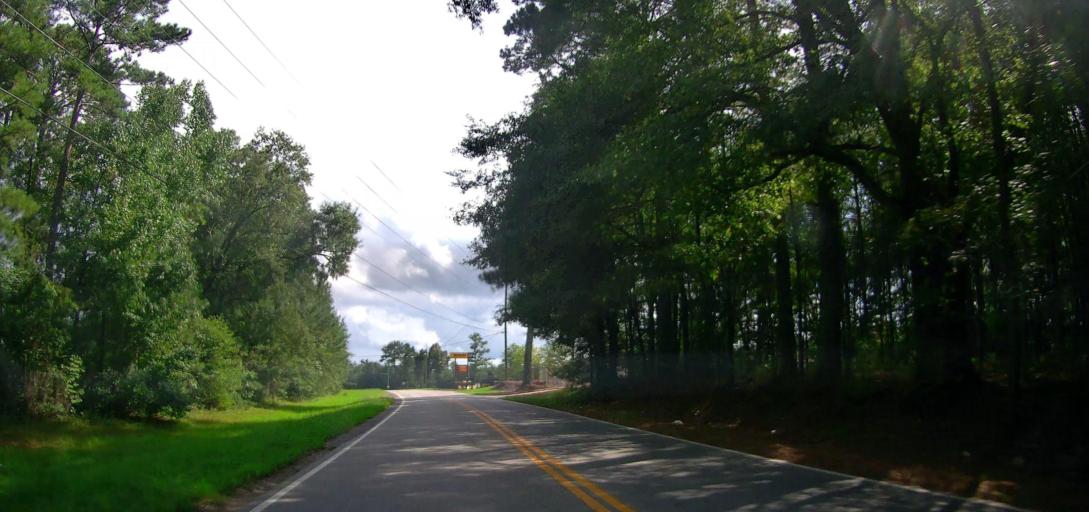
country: US
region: Alabama
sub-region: Russell County
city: Phenix City
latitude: 32.5998
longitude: -84.9488
